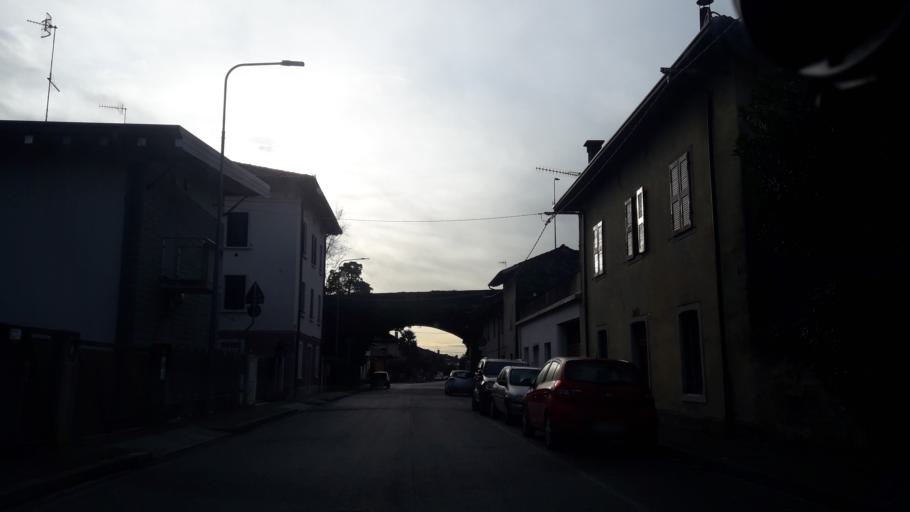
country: IT
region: Friuli Venezia Giulia
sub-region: Provincia di Udine
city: Udine
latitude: 46.0722
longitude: 13.2471
